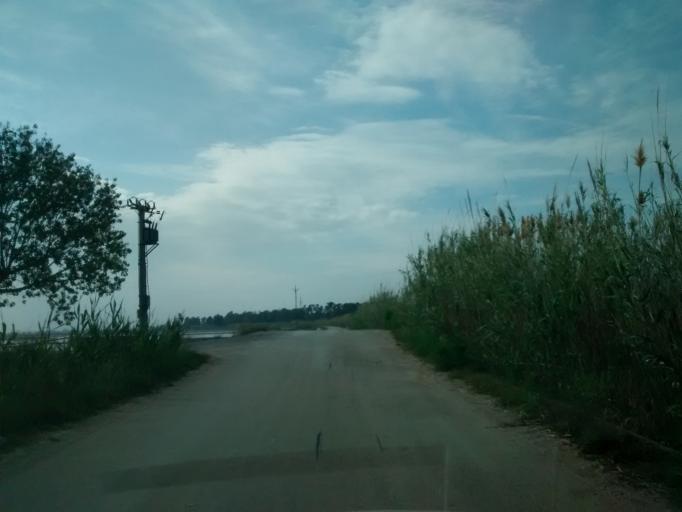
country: ES
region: Catalonia
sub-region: Provincia de Tarragona
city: Deltebre
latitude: 40.6945
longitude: 0.8386
